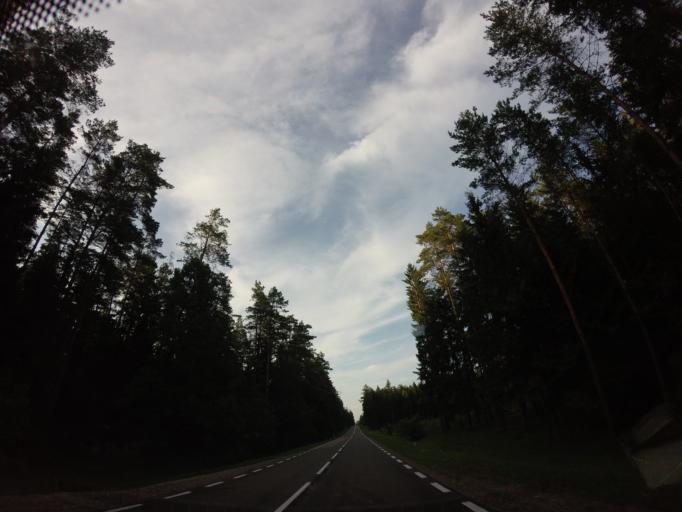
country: PL
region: Podlasie
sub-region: Powiat sejnenski
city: Sejny
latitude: 53.9908
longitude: 23.3043
